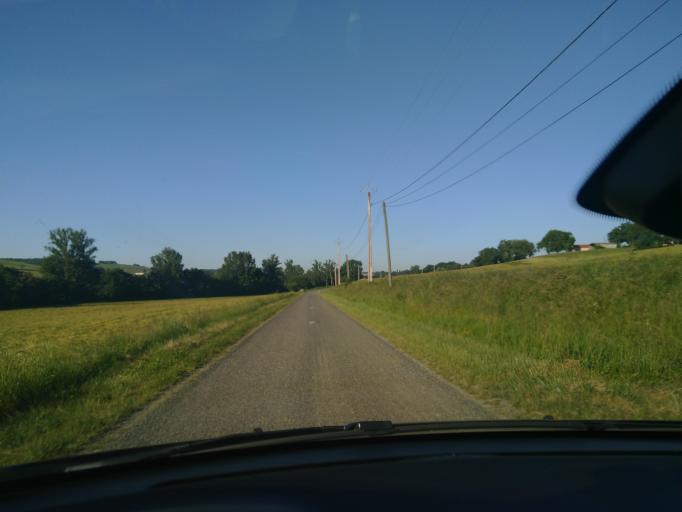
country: FR
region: Midi-Pyrenees
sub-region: Departement du Tarn-et-Garonne
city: Beaumont-de-Lomagne
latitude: 43.8211
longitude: 1.0489
